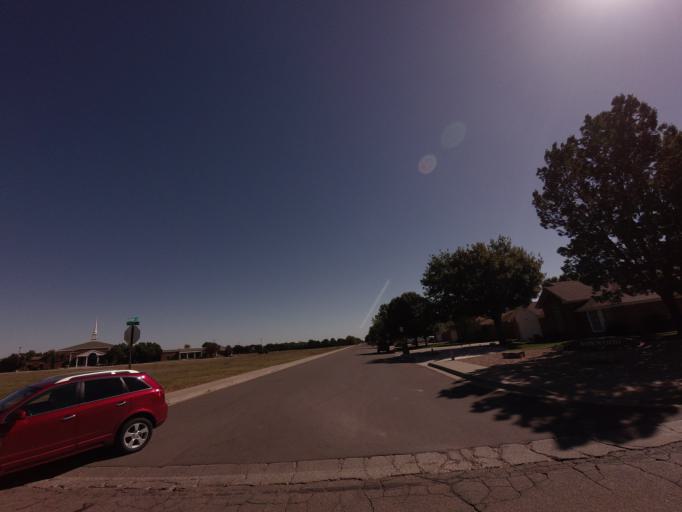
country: US
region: New Mexico
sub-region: Curry County
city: Clovis
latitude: 34.4232
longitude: -103.1785
